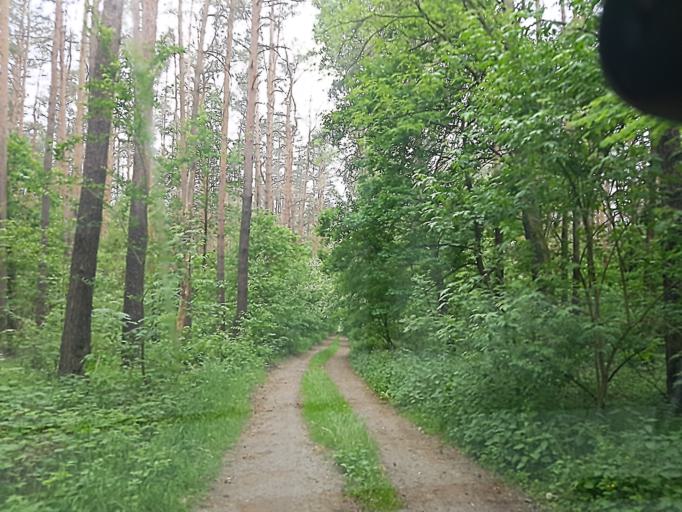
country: DE
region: Brandenburg
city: Finsterwalde
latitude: 51.5976
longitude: 13.7215
